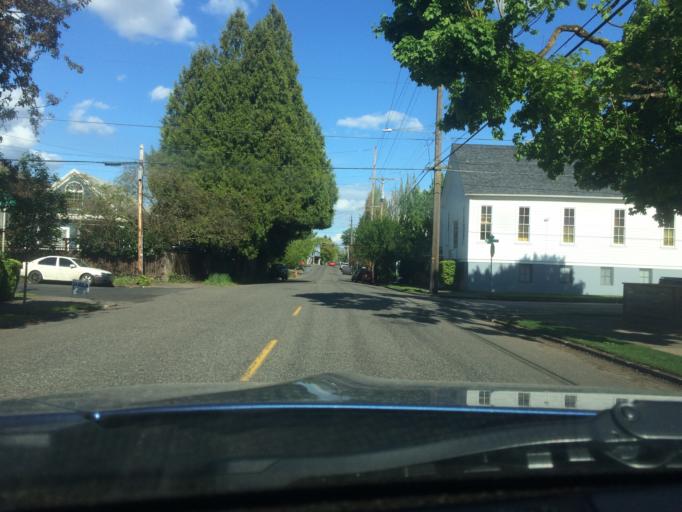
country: US
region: Oregon
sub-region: Multnomah County
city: Portland
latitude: 45.5546
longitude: -122.6642
